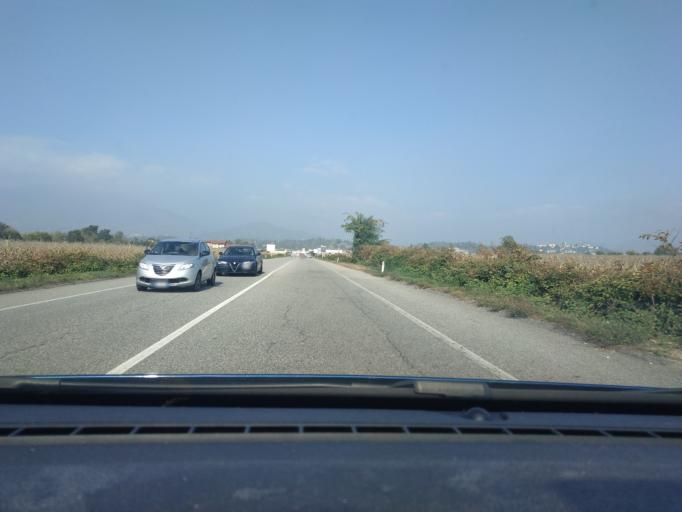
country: IT
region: Piedmont
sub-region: Provincia di Biella
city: Ponderano
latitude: 45.5419
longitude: 8.0377
